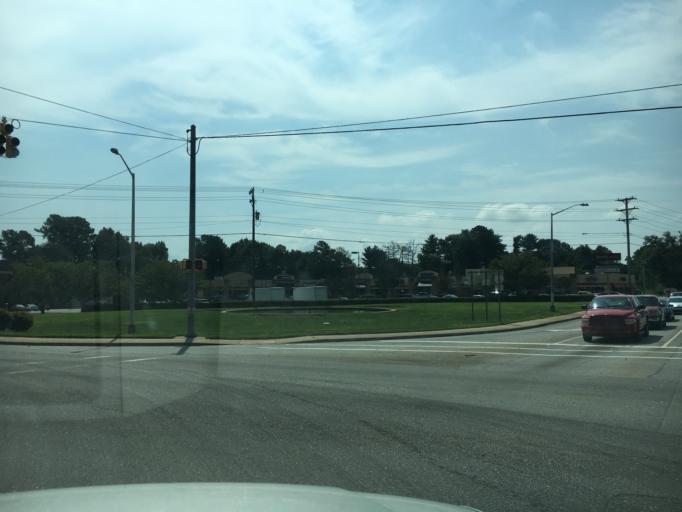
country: US
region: South Carolina
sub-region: Spartanburg County
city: Arcadia
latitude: 34.9224
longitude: -81.9868
